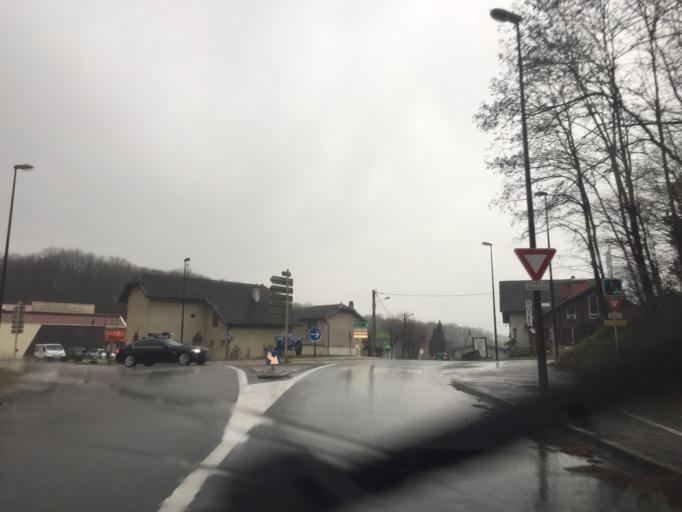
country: FR
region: Franche-Comte
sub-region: Departement du Jura
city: Mouchard
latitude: 46.9783
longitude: 5.8073
